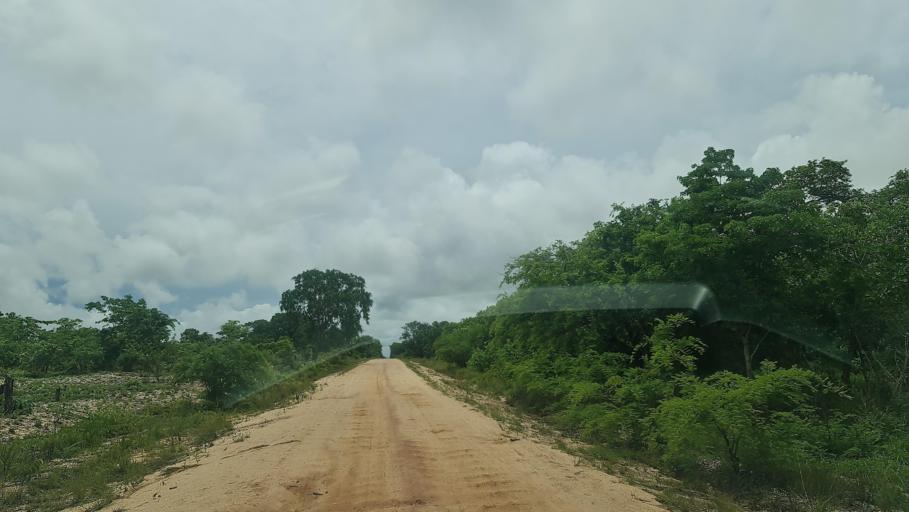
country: MZ
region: Zambezia
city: Quelimane
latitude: -17.2541
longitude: 37.2228
